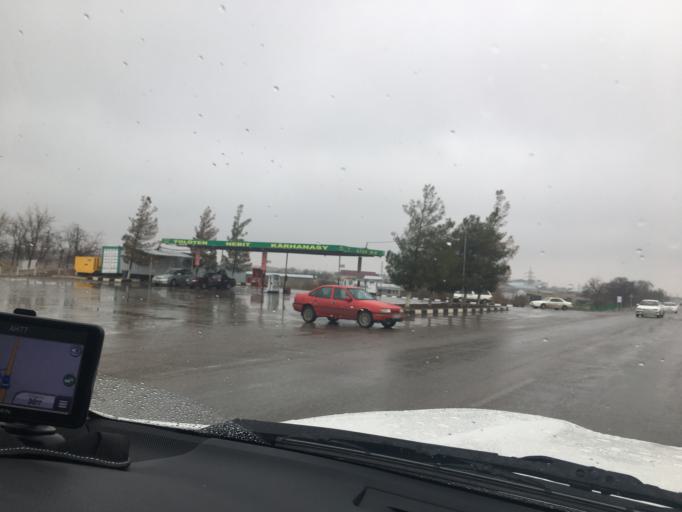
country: TM
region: Mary
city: Yoloeten
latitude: 37.2901
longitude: 62.3437
